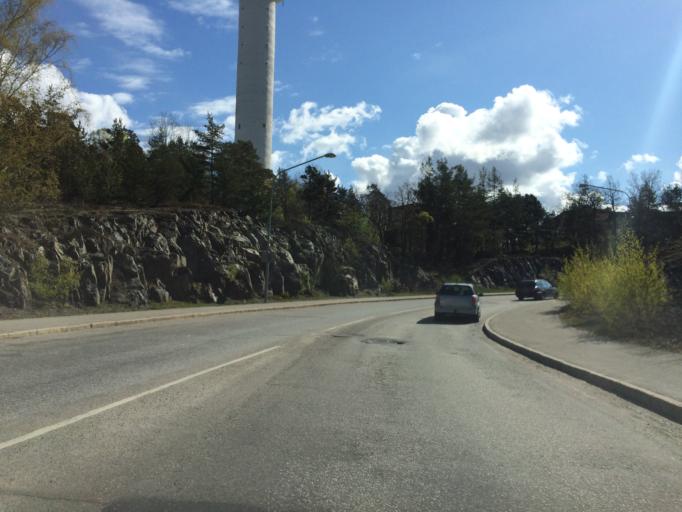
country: SE
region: Stockholm
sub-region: Huddinge Kommun
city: Segeltorp
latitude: 59.2964
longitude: 17.9422
